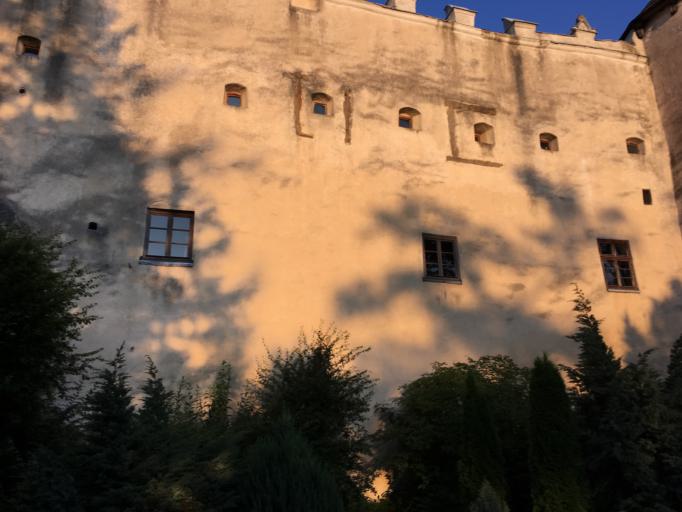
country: PL
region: Lesser Poland Voivodeship
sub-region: Powiat nowotarski
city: Niedzica
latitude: 49.4225
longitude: 20.3192
